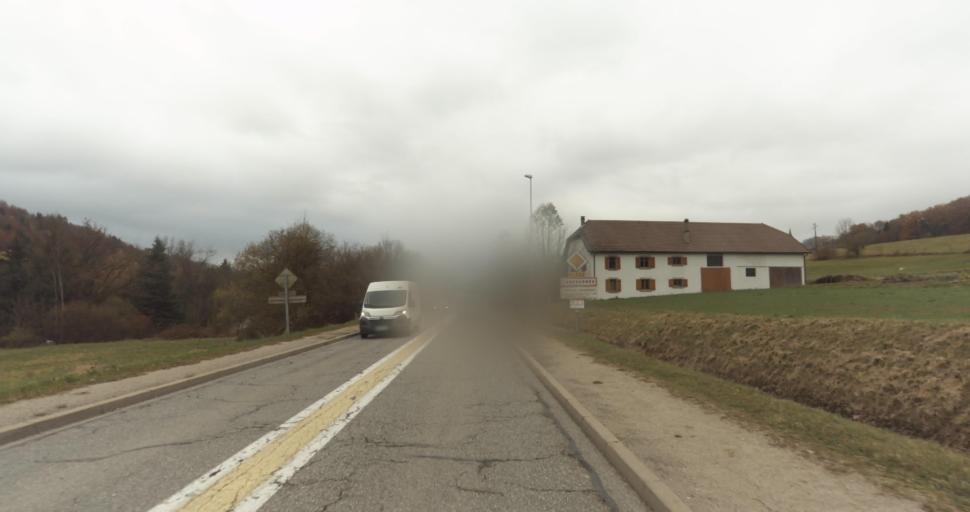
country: FR
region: Rhone-Alpes
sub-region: Departement de la Haute-Savoie
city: Saint-Martin-Bellevue
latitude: 45.9810
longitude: 6.1648
